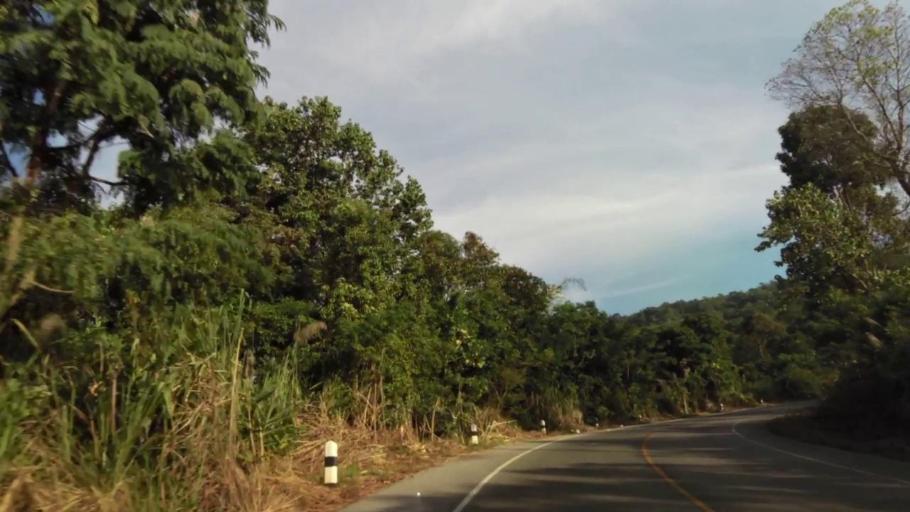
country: TH
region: Chiang Rai
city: Khun Tan
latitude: 19.8628
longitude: 100.4297
